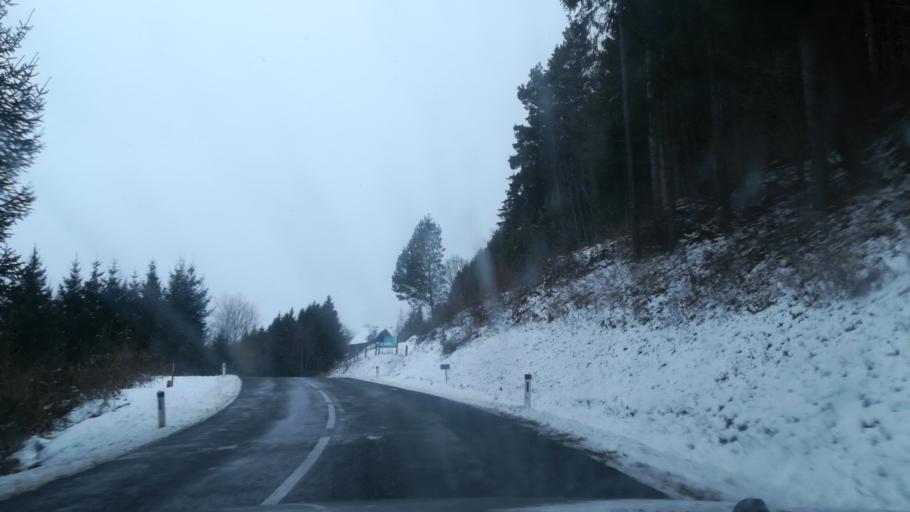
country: AT
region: Styria
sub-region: Politischer Bezirk Murtal
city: Poels
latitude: 47.2114
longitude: 14.5435
